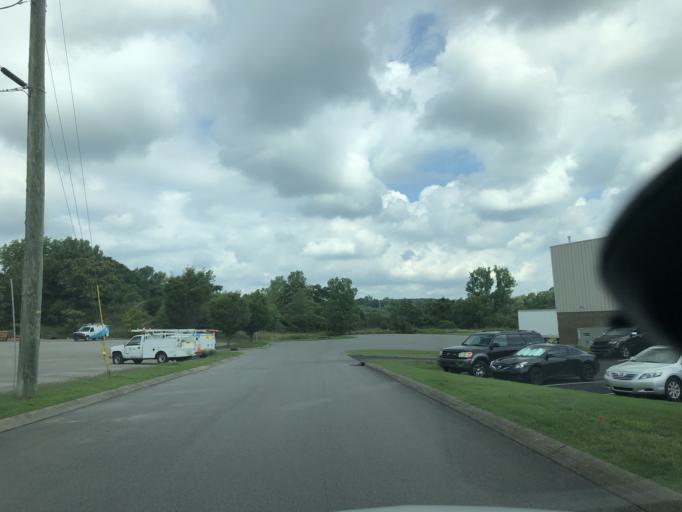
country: US
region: Tennessee
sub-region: Rutherford County
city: La Vergne
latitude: 36.0153
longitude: -86.6084
